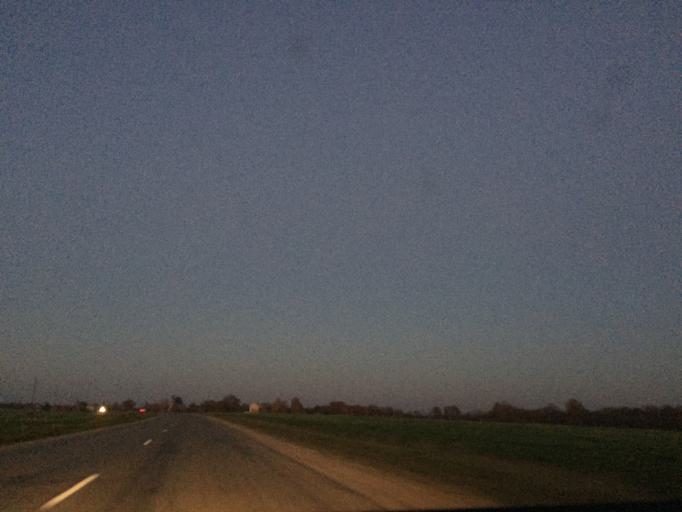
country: LV
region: Tervete
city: Zelmeni
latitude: 56.4991
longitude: 23.2579
